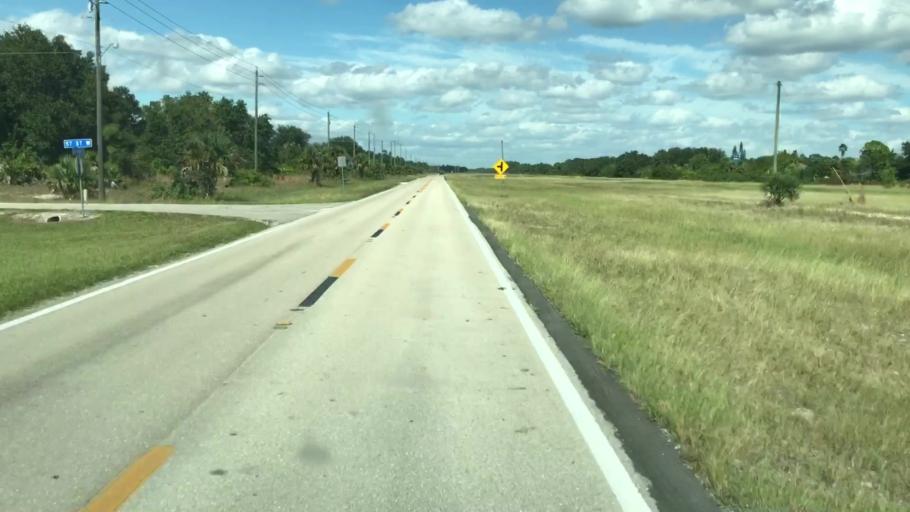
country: US
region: Florida
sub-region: Lee County
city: Lehigh Acres
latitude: 26.6678
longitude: -81.6636
